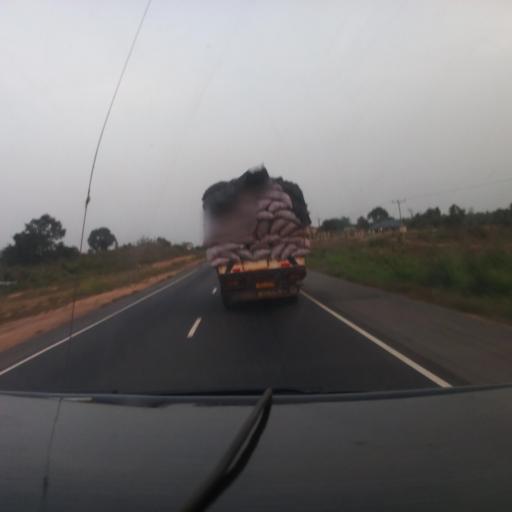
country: GH
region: Eastern
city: Nsawam
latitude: 5.8847
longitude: -0.3775
